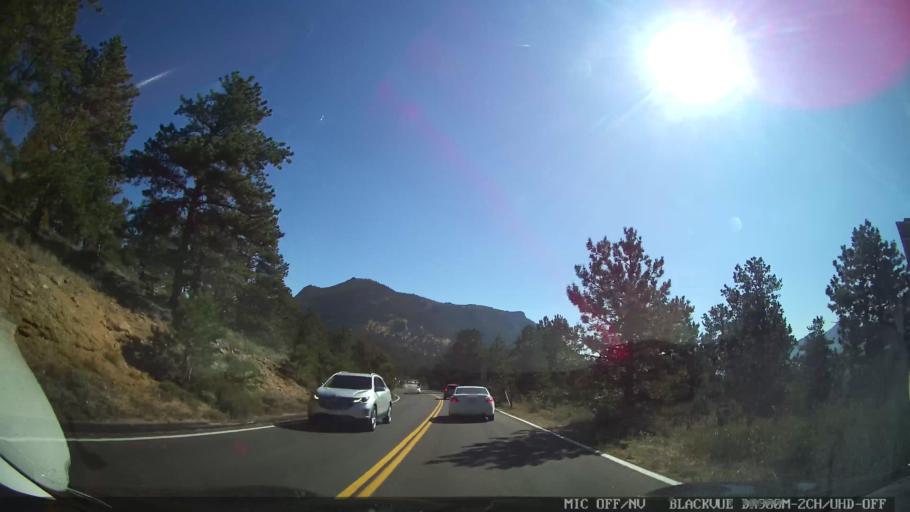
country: US
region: Colorado
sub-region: Larimer County
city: Estes Park
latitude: 40.3875
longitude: -105.6138
